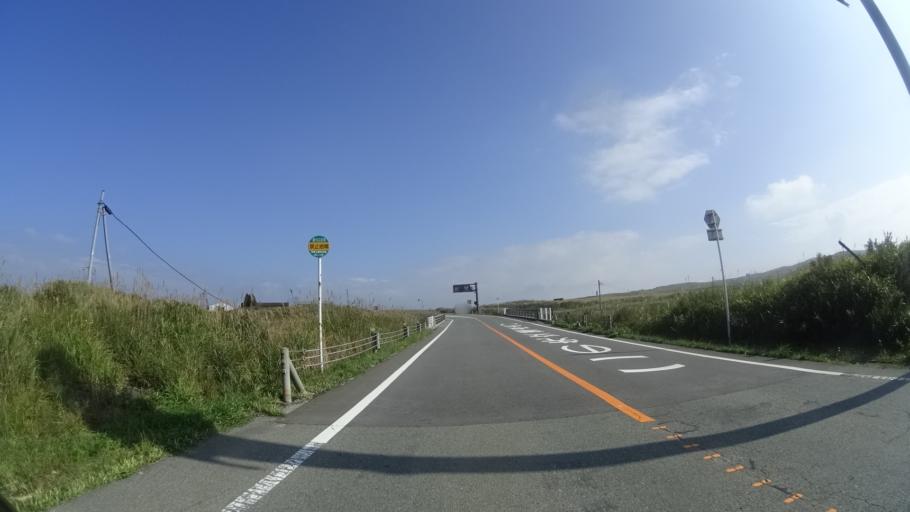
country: JP
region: Kumamoto
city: Aso
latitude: 33.0095
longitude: 131.0657
